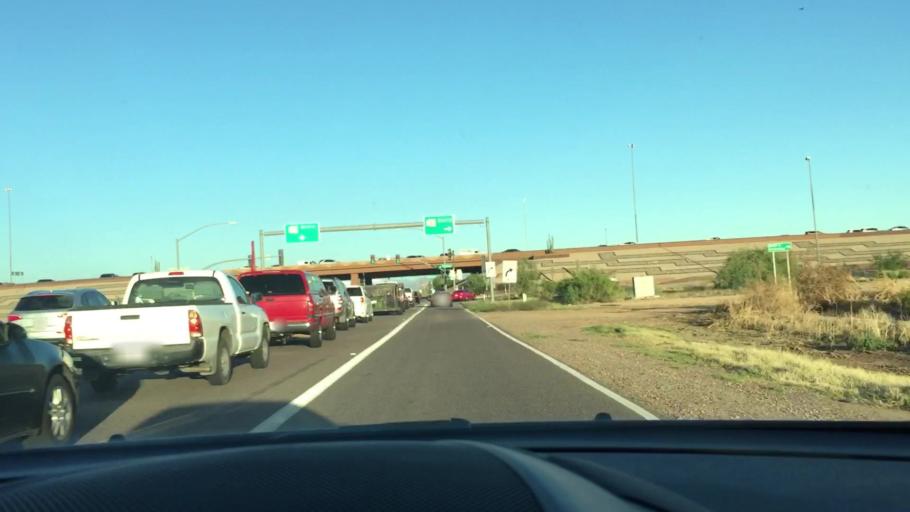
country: US
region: Arizona
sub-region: Maricopa County
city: Tempe
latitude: 33.4512
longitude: -111.8924
